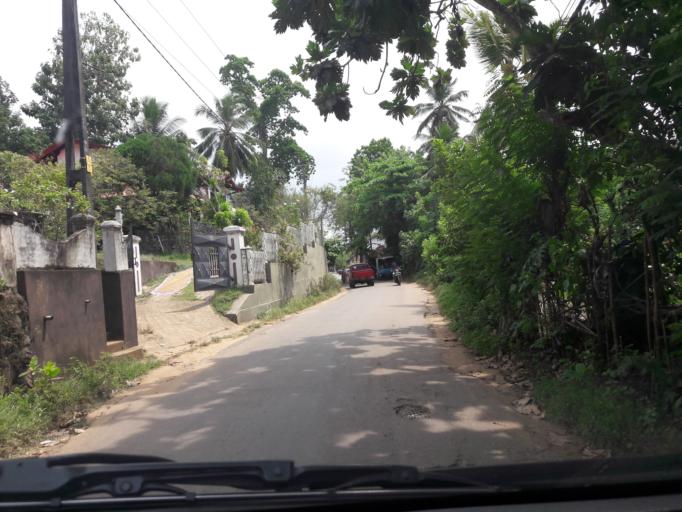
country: LK
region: Southern
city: Hikkaduwa
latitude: 6.0961
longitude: 80.1514
